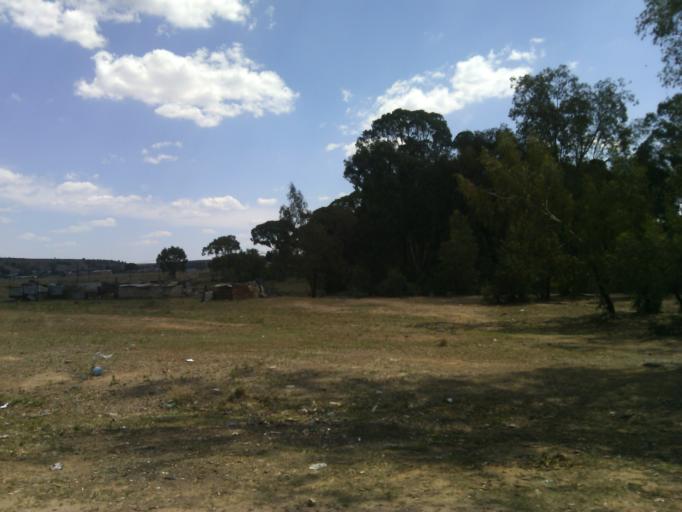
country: ZA
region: Orange Free State
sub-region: Xhariep District Municipality
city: Dewetsdorp
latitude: -29.5757
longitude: 26.6800
